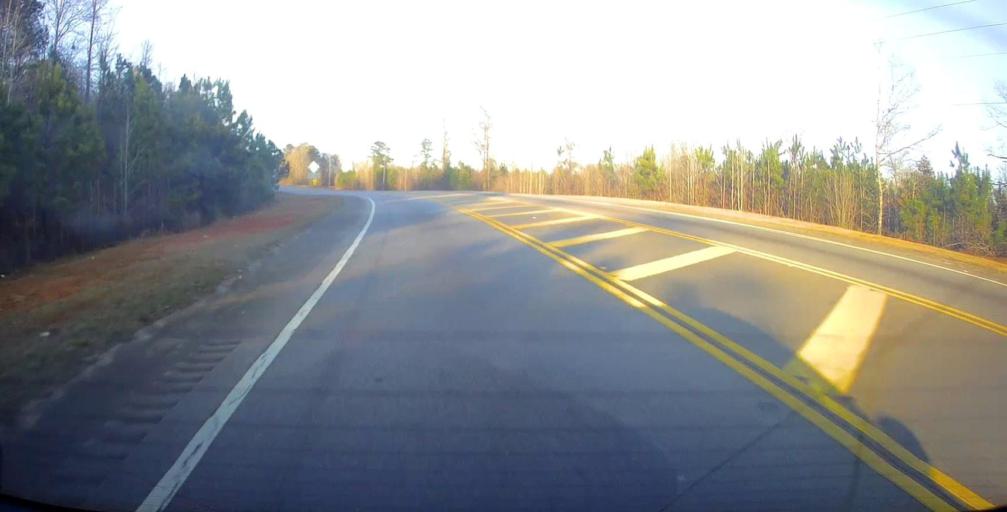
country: US
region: Georgia
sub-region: Troup County
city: La Grange
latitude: 32.9902
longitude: -85.0371
